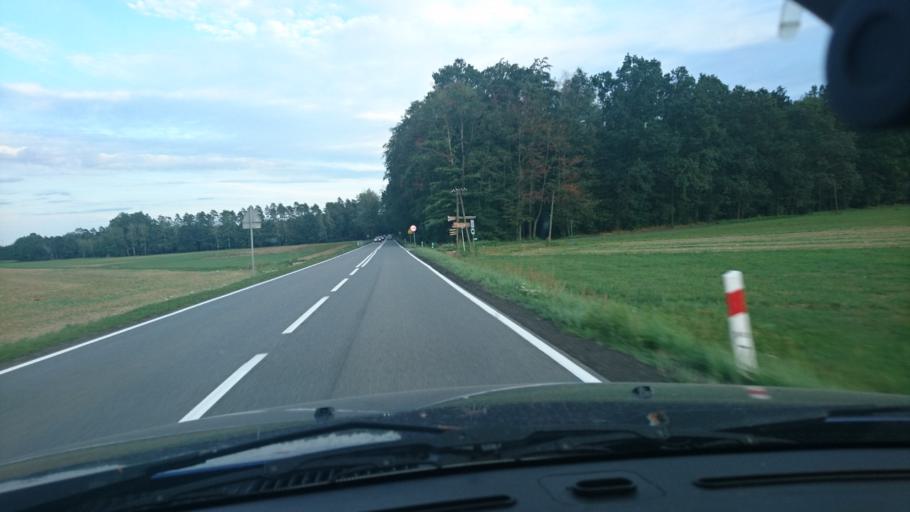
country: PL
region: Opole Voivodeship
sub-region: Powiat oleski
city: Olesno
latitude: 50.8532
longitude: 18.4650
